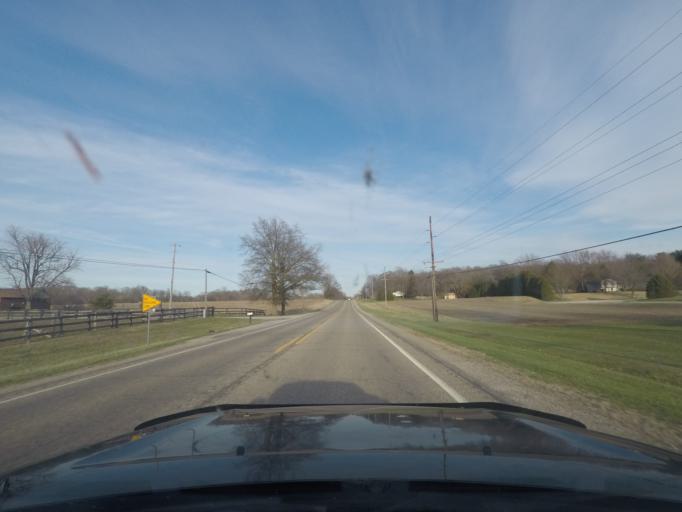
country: US
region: Indiana
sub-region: LaPorte County
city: LaPorte
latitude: 41.5914
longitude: -86.7821
